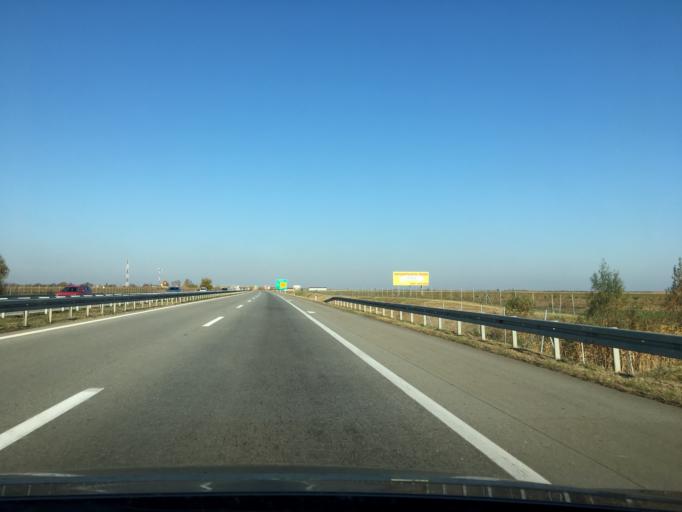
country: RS
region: Autonomna Pokrajina Vojvodina
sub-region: Juznobacki Okrug
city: Kovilj
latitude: 45.2332
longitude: 20.0479
